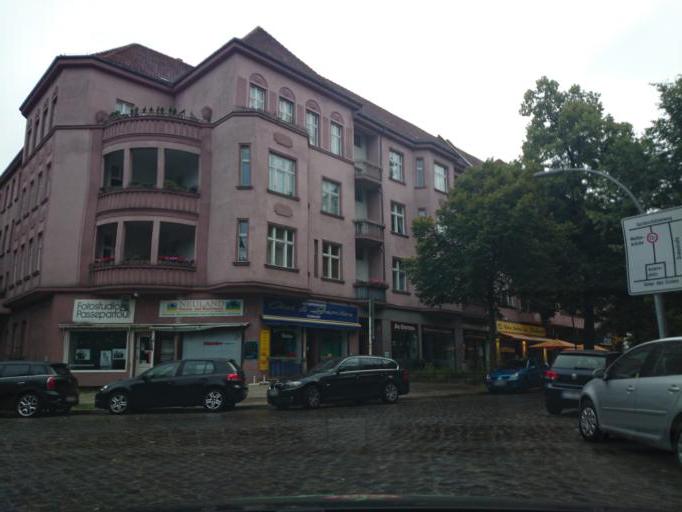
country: DE
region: Berlin
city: Lichterfelde
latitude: 52.4486
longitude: 13.3046
